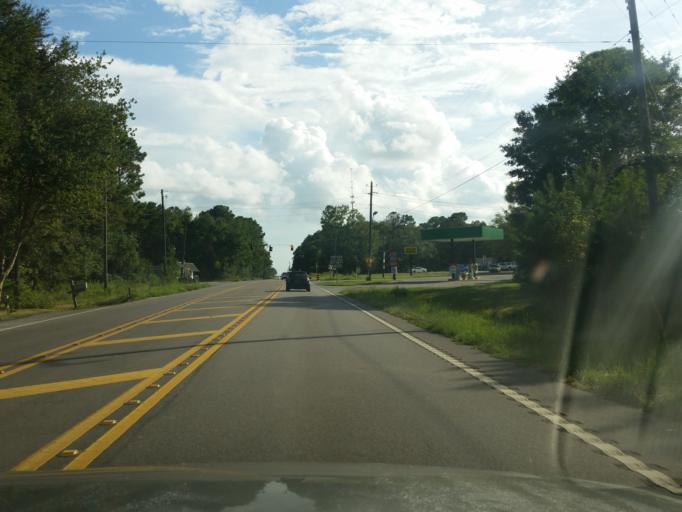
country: US
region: Alabama
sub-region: Mobile County
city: Dauphin Island
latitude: 30.3636
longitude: -88.1144
